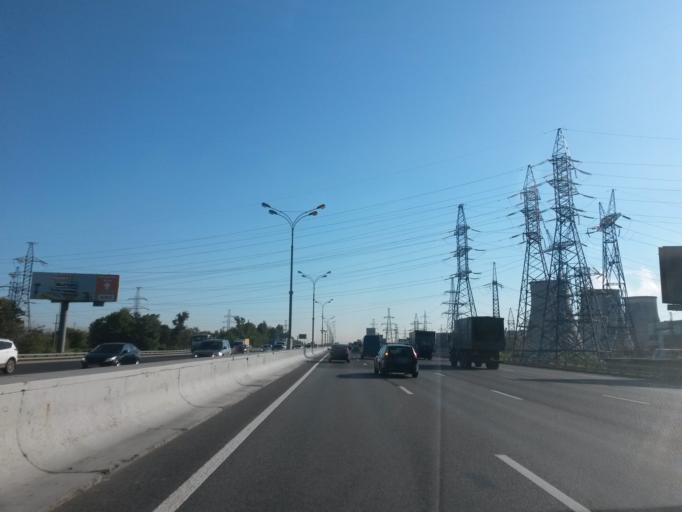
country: RU
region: Moskovskaya
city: Alekseyevka
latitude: 55.6353
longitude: 37.8116
